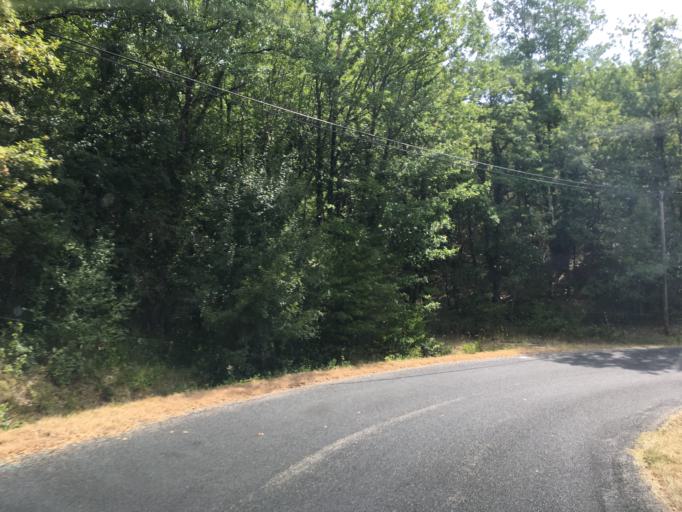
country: FR
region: Midi-Pyrenees
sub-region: Departement du Lot
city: Le Vigan
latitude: 44.7462
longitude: 1.5085
